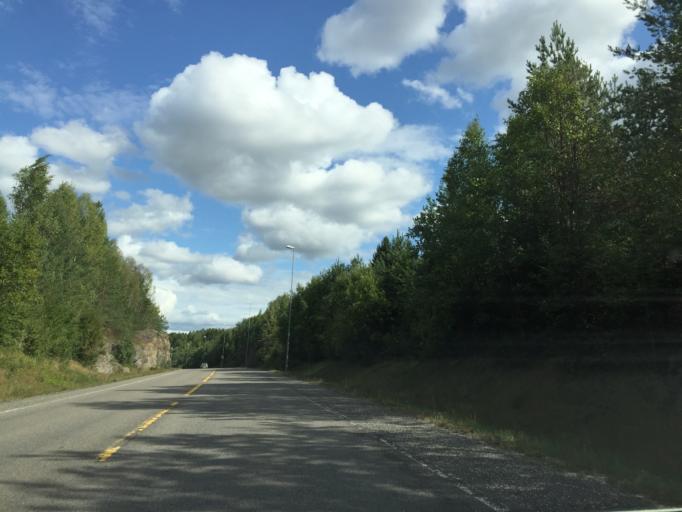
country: NO
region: Ostfold
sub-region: Hobol
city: Knappstad
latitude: 59.6166
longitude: 11.0426
